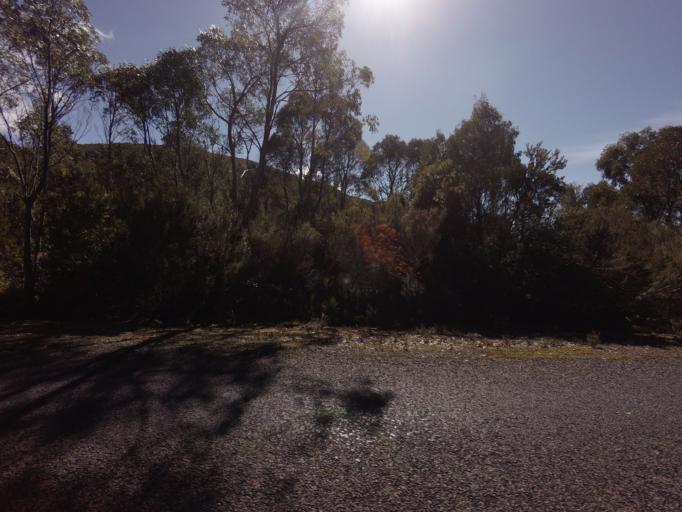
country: AU
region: Tasmania
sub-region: Derwent Valley
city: New Norfolk
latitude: -42.7236
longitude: 146.4472
